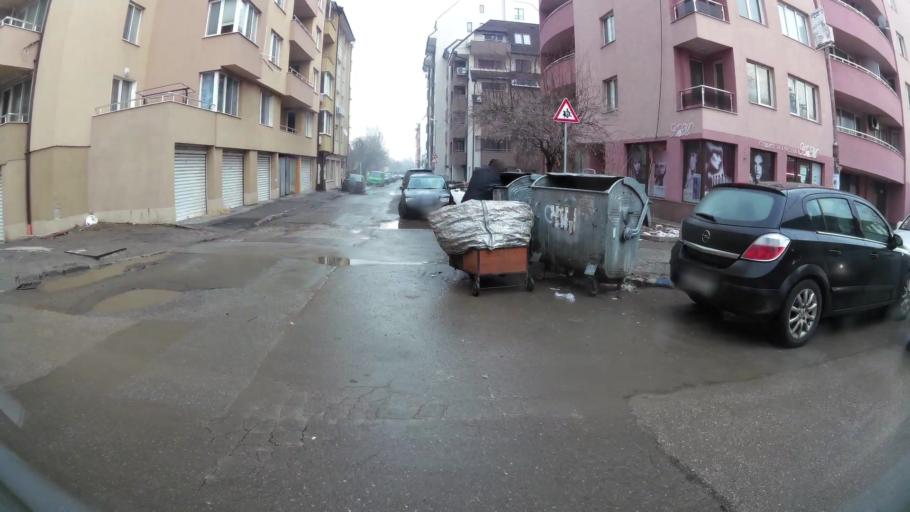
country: BG
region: Sofia-Capital
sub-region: Stolichna Obshtina
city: Sofia
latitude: 42.6910
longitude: 23.2839
